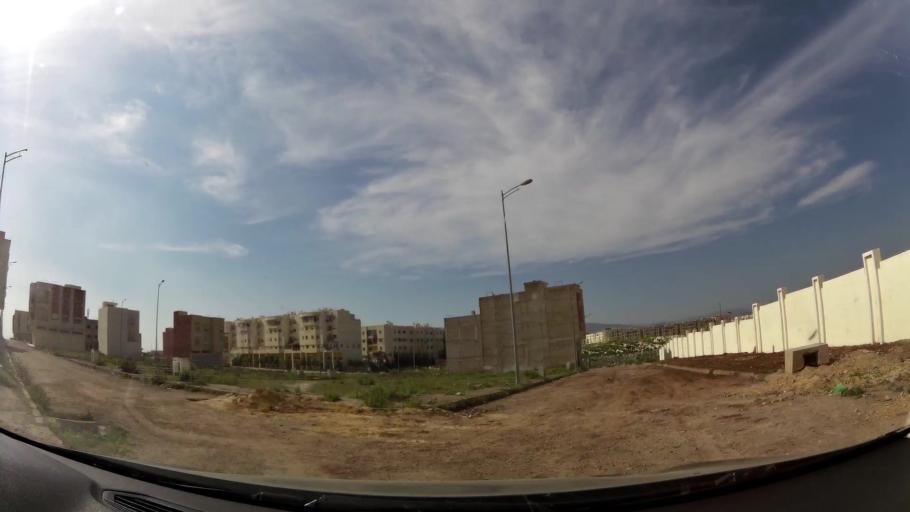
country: MA
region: Fes-Boulemane
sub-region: Fes
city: Fes
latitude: 34.0080
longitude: -5.0398
